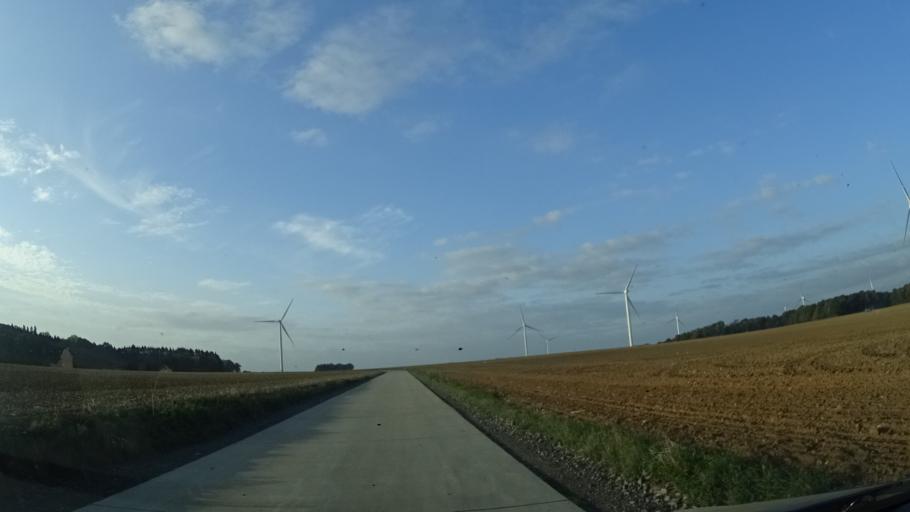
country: BE
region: Wallonia
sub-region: Province du Hainaut
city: Froidchapelle
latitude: 50.2210
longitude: 4.3374
